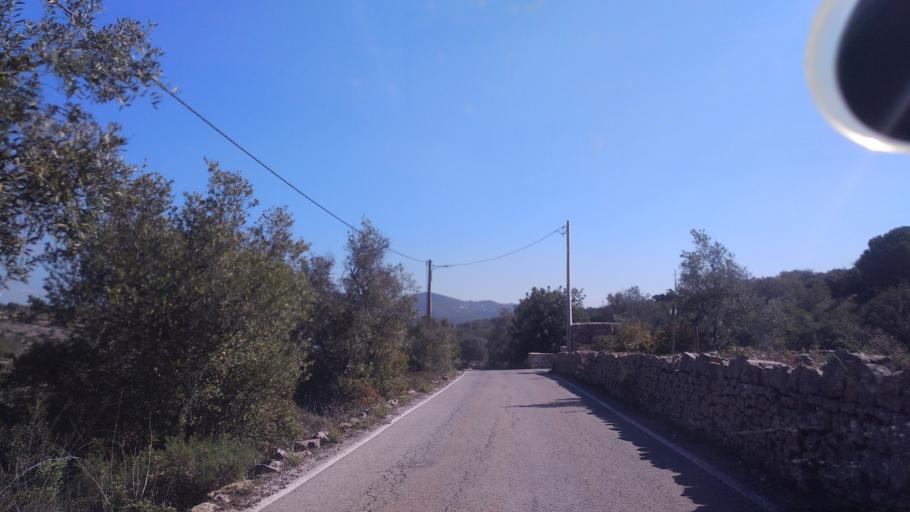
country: PT
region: Faro
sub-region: Faro
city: Santa Barbara de Nexe
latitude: 37.1116
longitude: -7.9307
